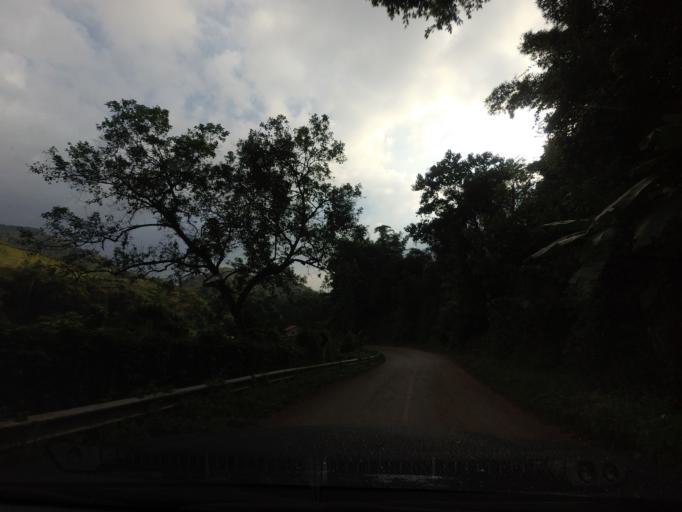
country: TH
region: Nan
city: Bo Kluea
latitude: 19.2718
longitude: 101.1782
